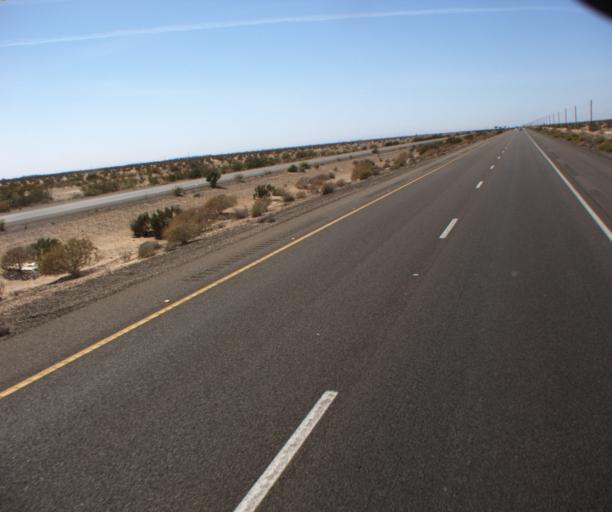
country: US
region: Arizona
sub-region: Yuma County
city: Somerton
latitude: 32.4948
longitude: -114.6644
